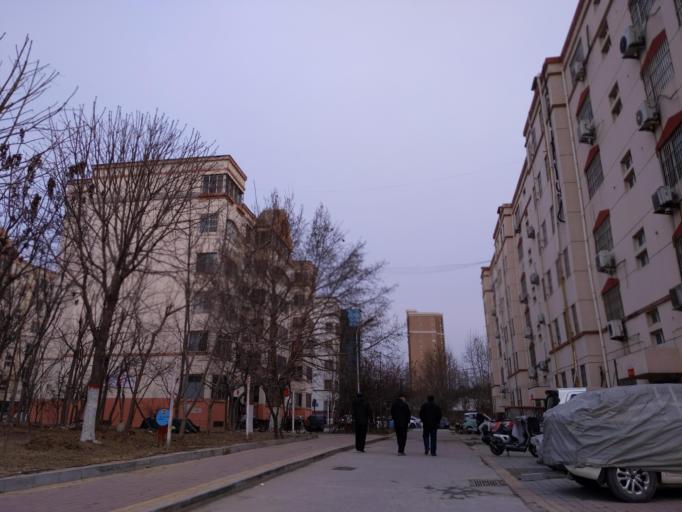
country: CN
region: Henan Sheng
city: Zhongyuanlu
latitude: 35.7553
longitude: 115.0536
